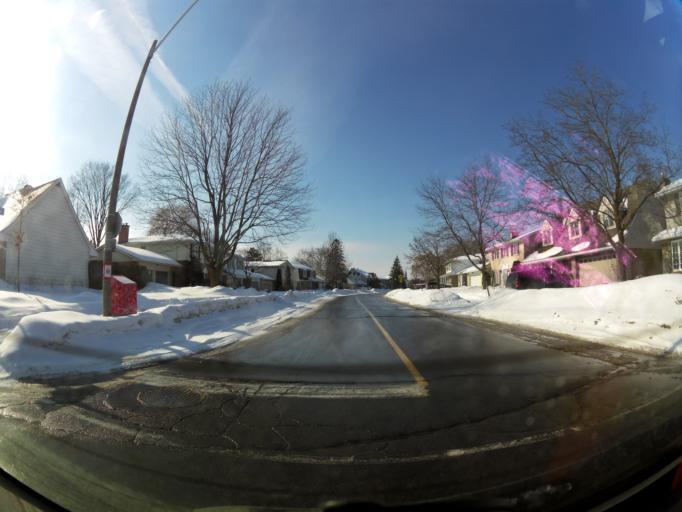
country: CA
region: Ontario
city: Ottawa
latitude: 45.3831
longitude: -75.6490
